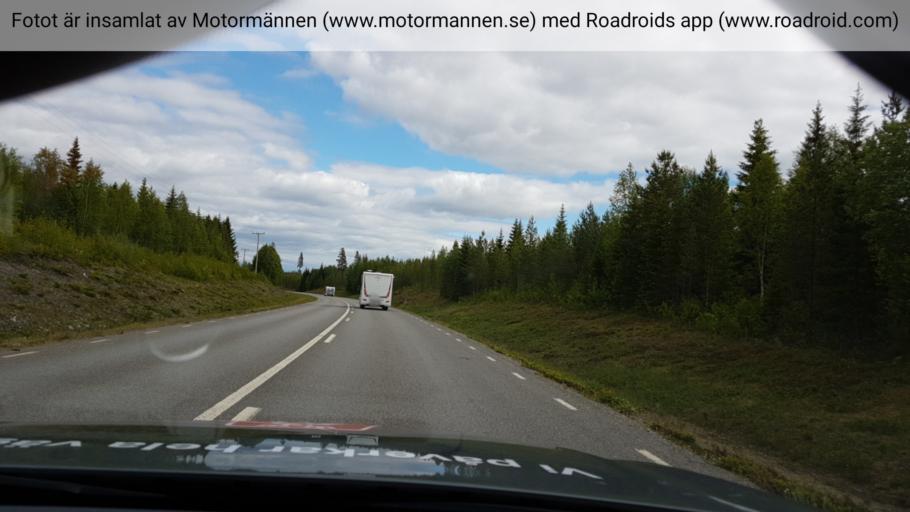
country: SE
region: Jaemtland
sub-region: Stroemsunds Kommun
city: Stroemsund
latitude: 64.2358
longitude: 15.4599
